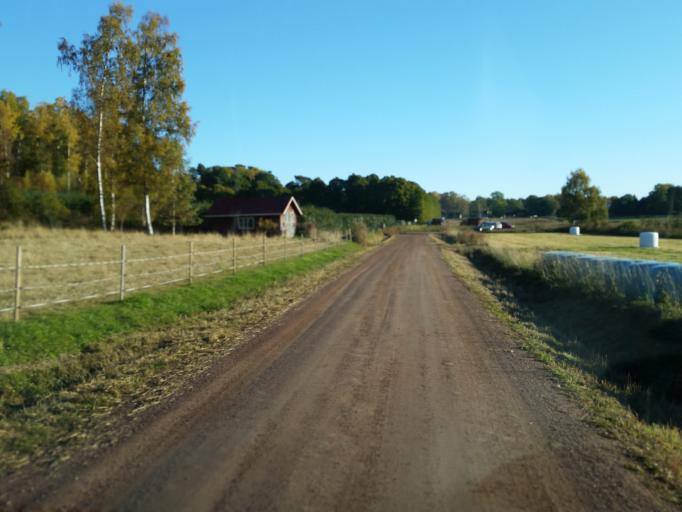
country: AX
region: Alands skaergard
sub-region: Vardoe
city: Vardoe
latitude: 60.2428
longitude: 20.3389
